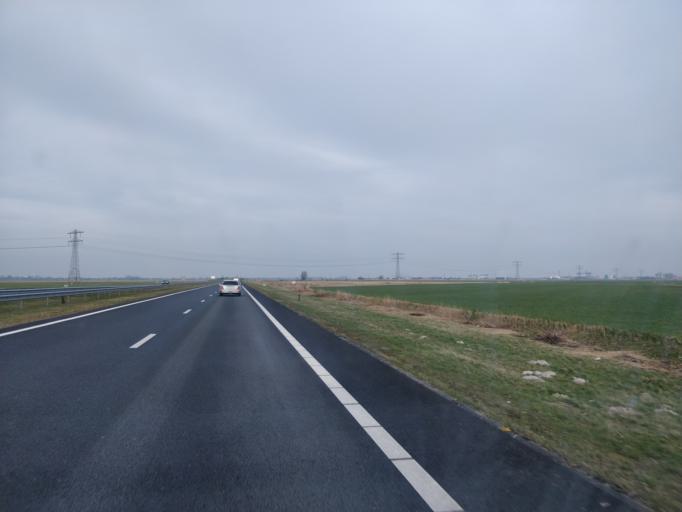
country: NL
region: Friesland
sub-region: Gemeente Leeuwarden
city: Goutum
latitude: 53.1641
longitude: 5.7722
